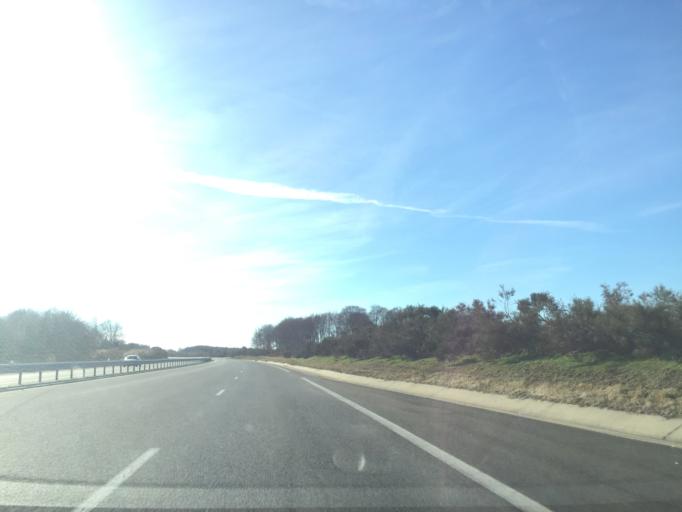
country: FR
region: Auvergne
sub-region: Departement du Puy-de-Dome
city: Gelles
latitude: 45.7281
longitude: 2.6966
